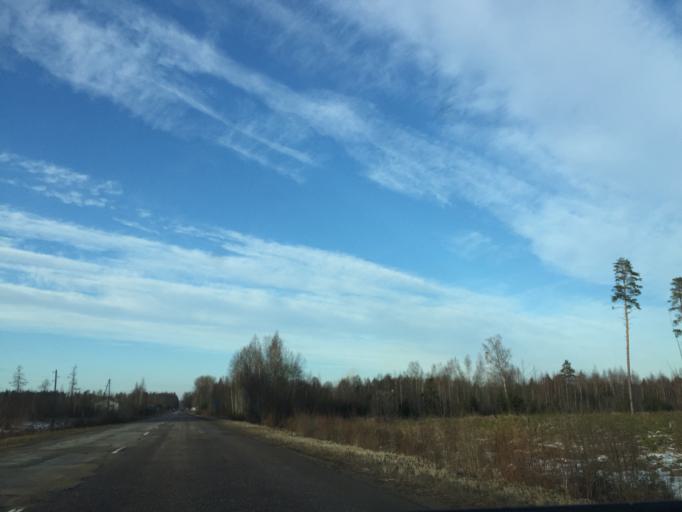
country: LV
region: Kekava
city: Balozi
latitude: 56.7293
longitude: 24.1101
